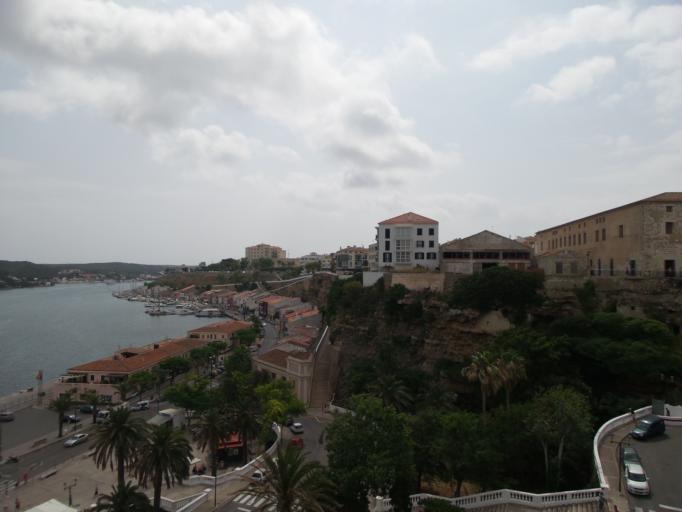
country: ES
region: Balearic Islands
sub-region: Illes Balears
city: Mao
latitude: 39.8898
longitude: 4.2655
